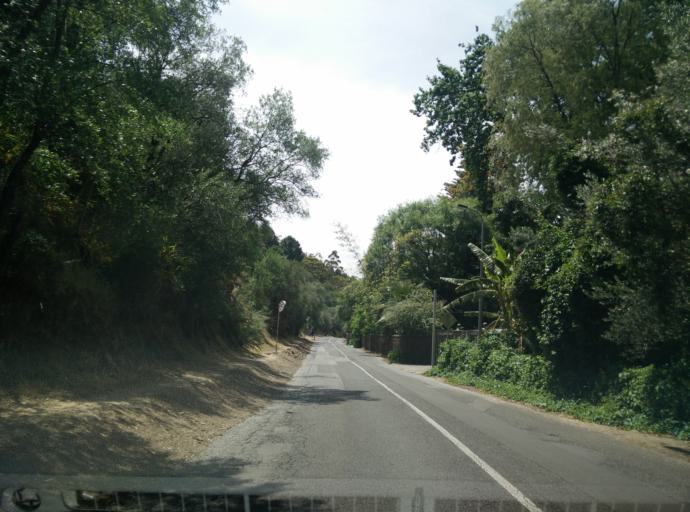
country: AU
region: South Australia
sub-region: Burnside
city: Beaumont
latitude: -34.9576
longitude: 138.6736
